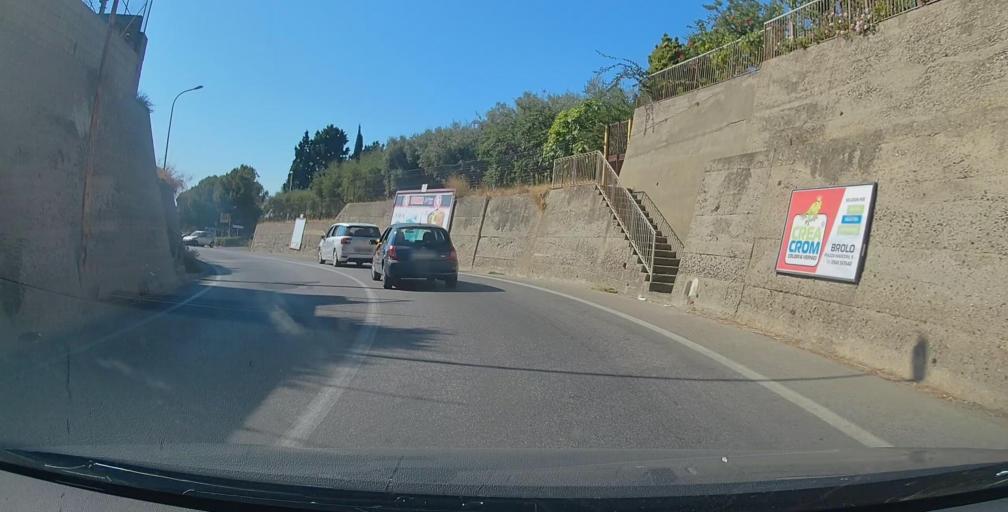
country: IT
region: Sicily
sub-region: Messina
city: Capo d'Orlando
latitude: 38.1557
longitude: 14.7520
